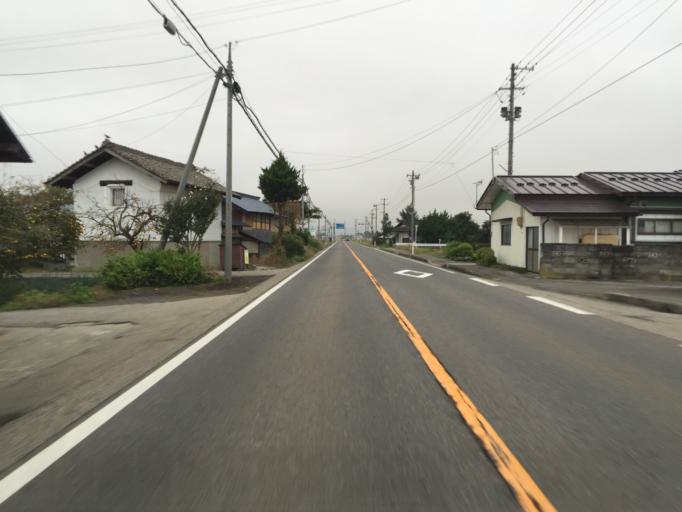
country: JP
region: Fukushima
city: Kitakata
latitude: 37.5301
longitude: 139.8852
